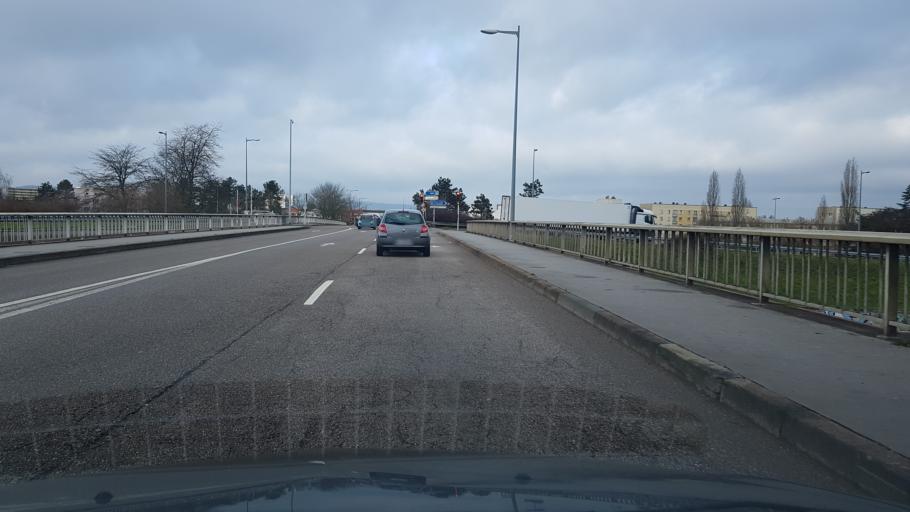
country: FR
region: Lorraine
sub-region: Departement de la Moselle
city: Metz
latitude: 49.1311
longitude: 6.1721
